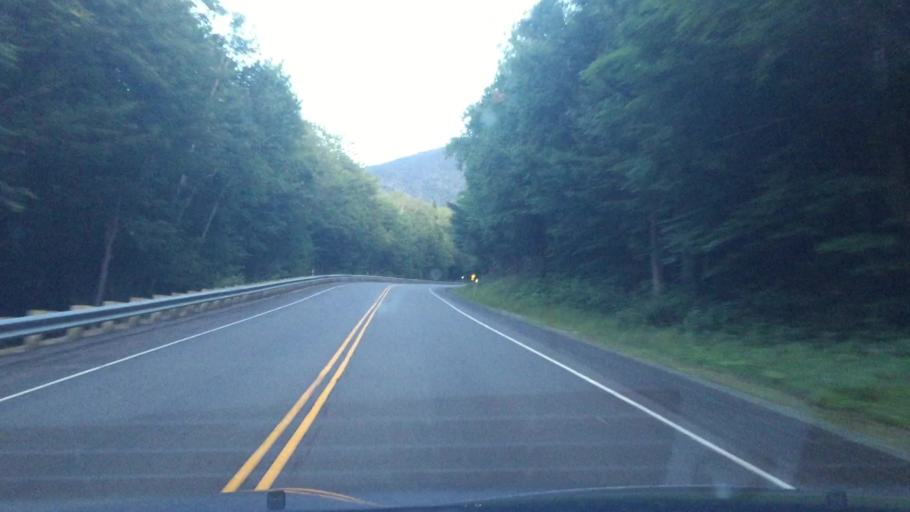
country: US
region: New Hampshire
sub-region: Grafton County
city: Woodstock
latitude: 44.0319
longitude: -71.5254
